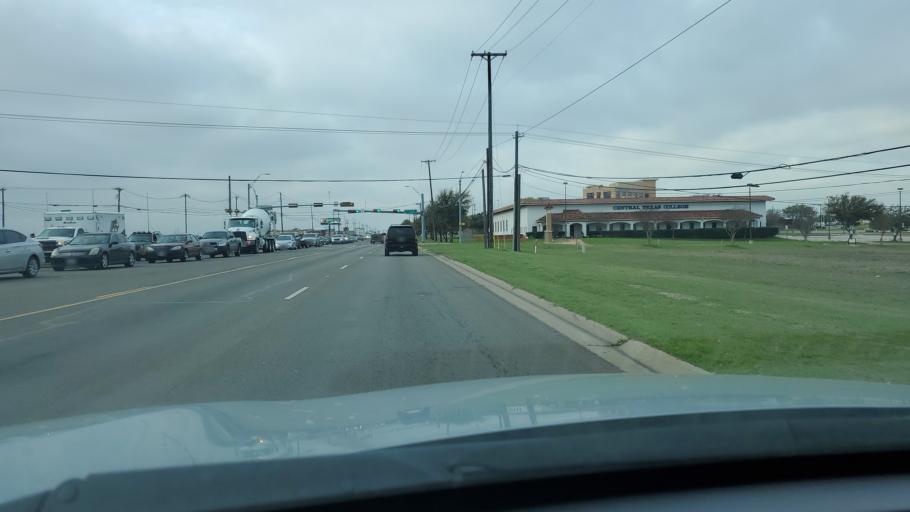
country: US
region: Texas
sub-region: Bell County
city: Fort Hood
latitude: 31.1174
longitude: -97.7980
